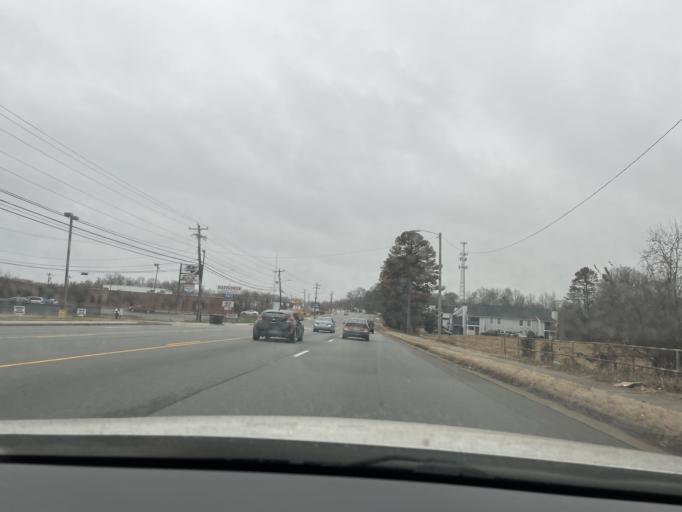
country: US
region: North Carolina
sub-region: Guilford County
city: Greensboro
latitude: 36.0294
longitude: -79.8018
